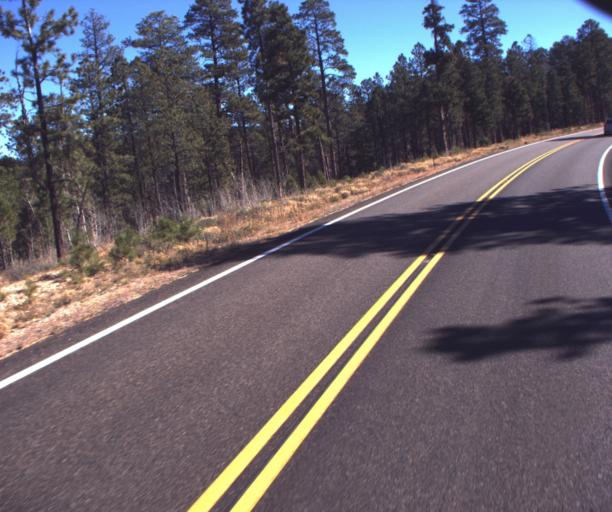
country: US
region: Arizona
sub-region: Coconino County
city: Fredonia
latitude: 36.6671
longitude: -112.1966
